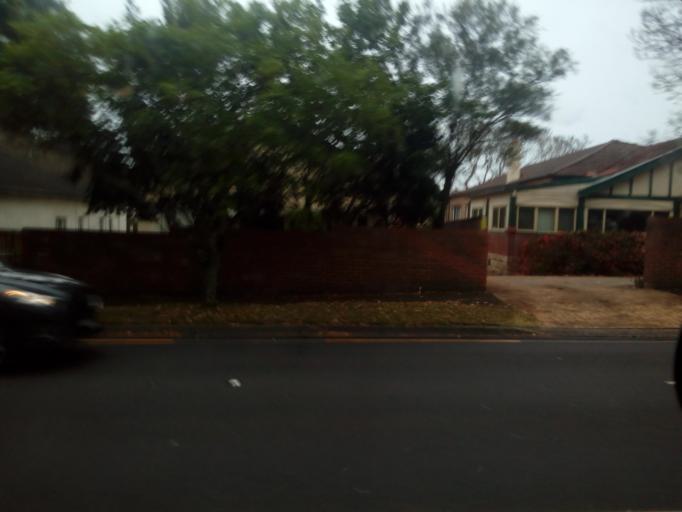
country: AU
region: New South Wales
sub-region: Willoughby
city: Chatswood
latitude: -33.7859
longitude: 151.1841
